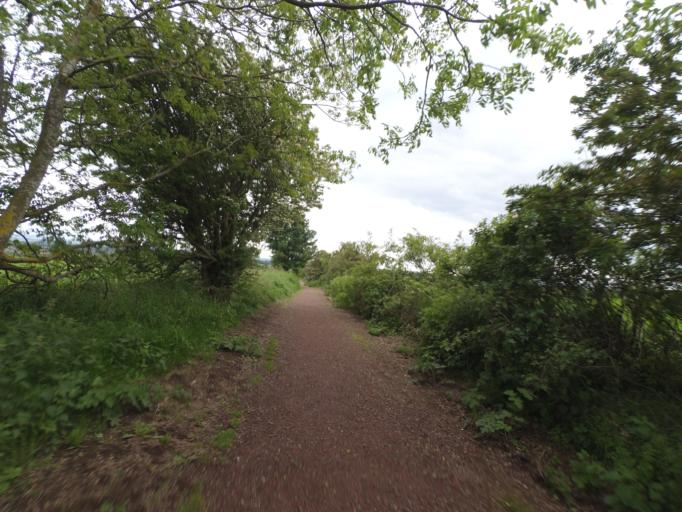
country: GB
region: Scotland
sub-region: East Lothian
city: Ormiston
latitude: 55.9180
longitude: -2.9676
